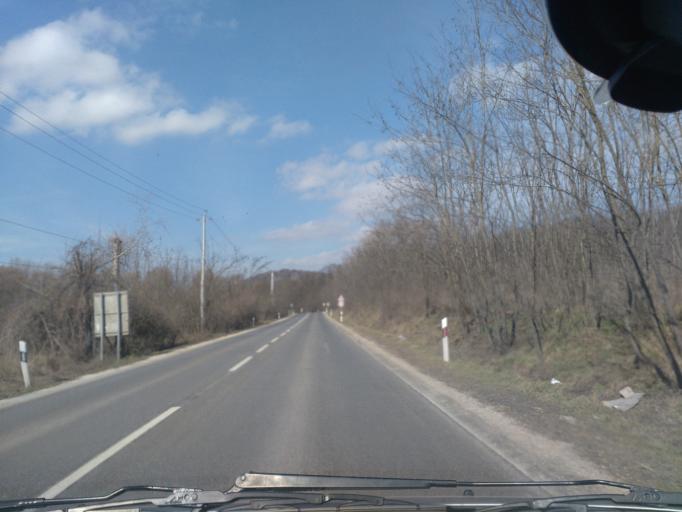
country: HU
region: Pest
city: Piliscsaba
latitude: 47.6487
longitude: 18.8037
